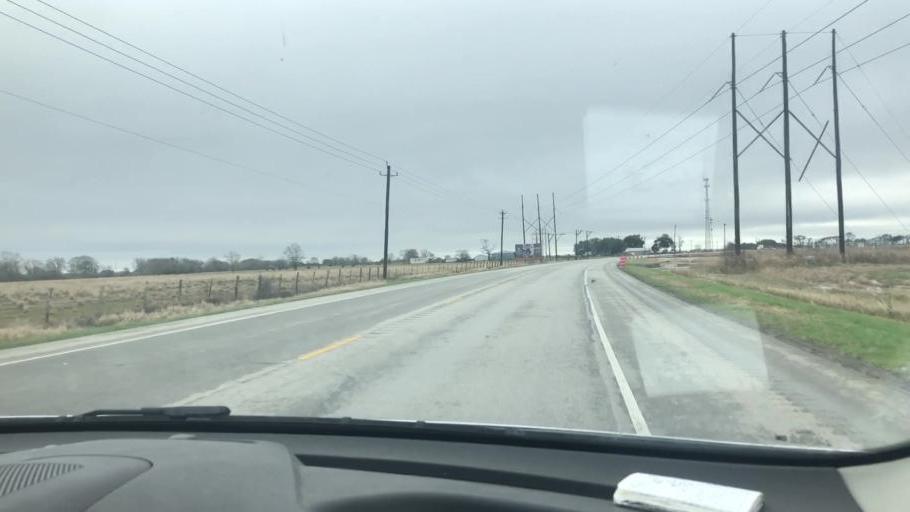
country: US
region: Texas
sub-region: Wharton County
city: Boling
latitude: 29.1445
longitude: -95.9879
